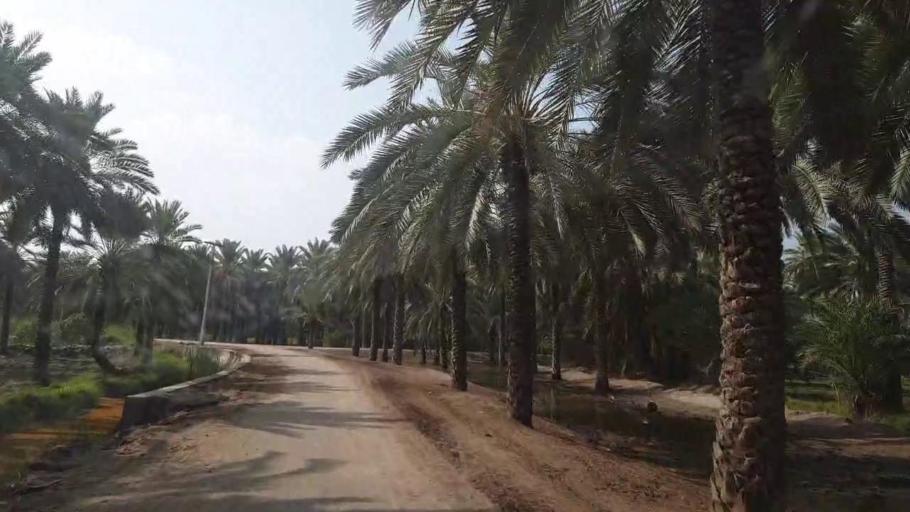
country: PK
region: Sindh
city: Khairpur
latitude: 27.5902
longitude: 68.7692
